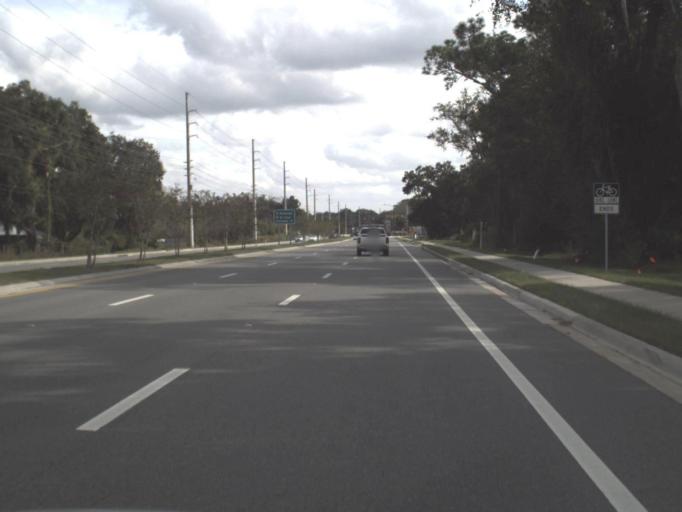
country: US
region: Florida
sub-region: Osceola County
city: Saint Cloud
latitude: 28.3507
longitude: -81.2348
